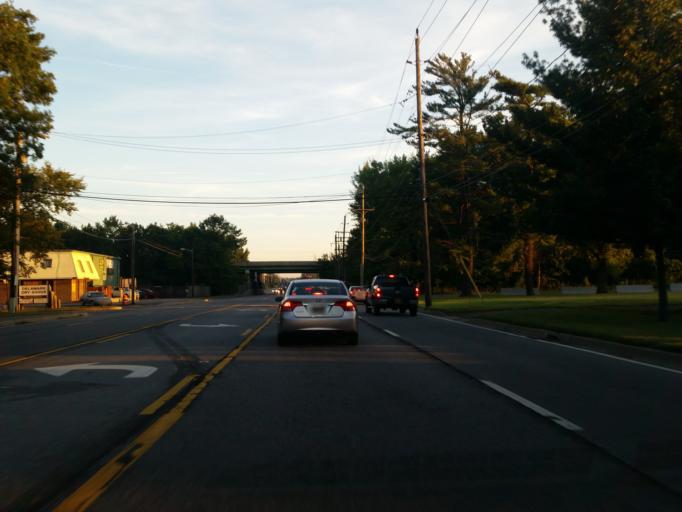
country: US
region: Delaware
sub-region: New Castle County
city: Brookside
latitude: 39.6471
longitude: -75.7315
